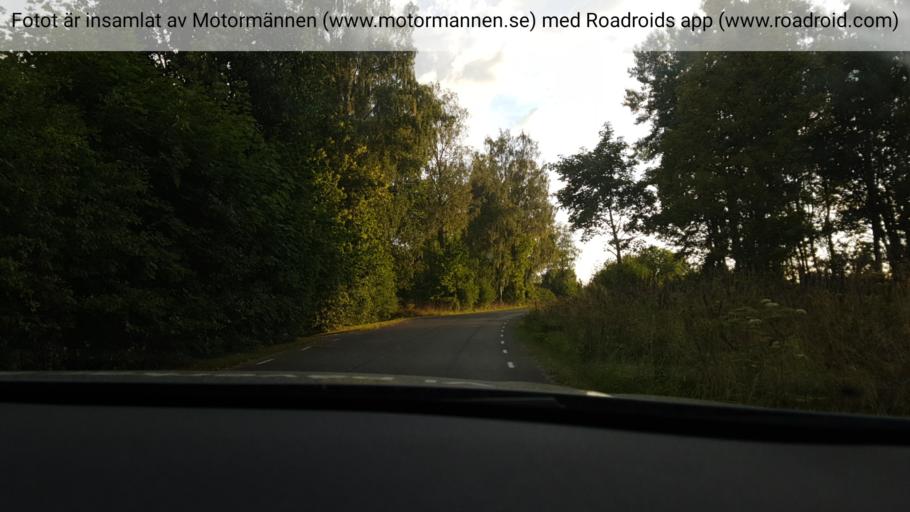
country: SE
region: Vaestra Goetaland
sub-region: Falkopings Kommun
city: Floby
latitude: 57.9913
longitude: 13.4272
